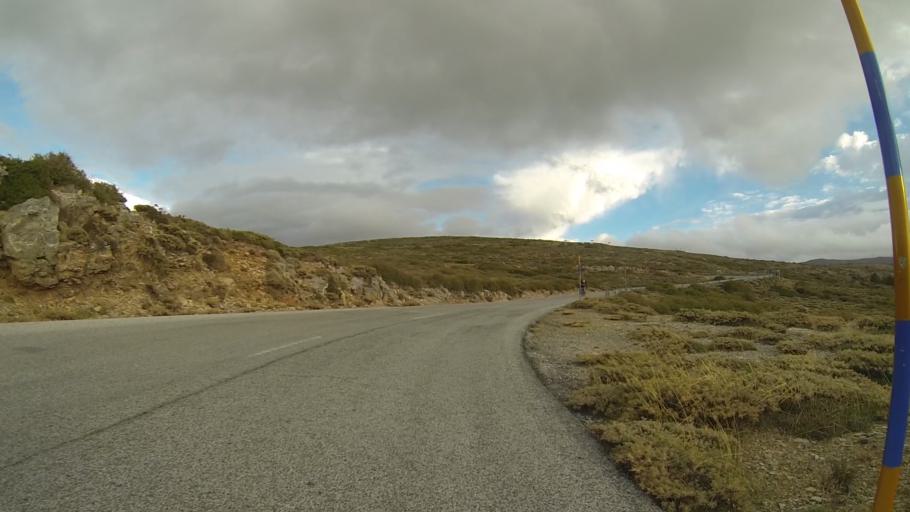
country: ES
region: Andalusia
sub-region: Provincia de Granada
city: Guejar-Sierra
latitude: 37.1222
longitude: -3.4332
